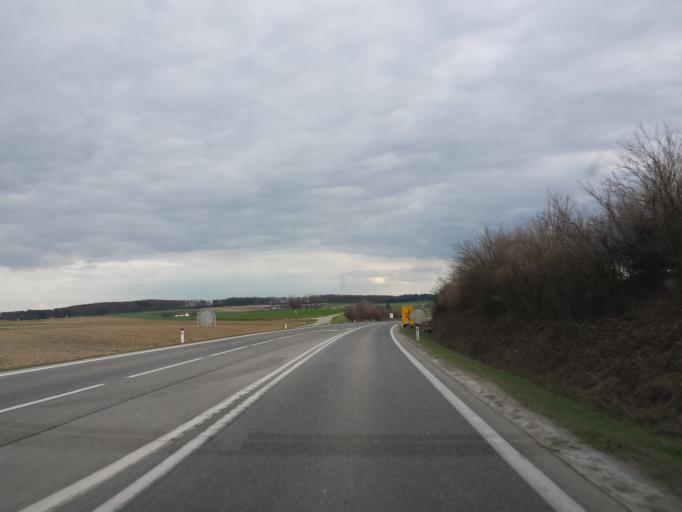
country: AT
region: Lower Austria
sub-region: Politischer Bezirk Krems
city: Gfohl
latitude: 48.5179
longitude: 15.5065
